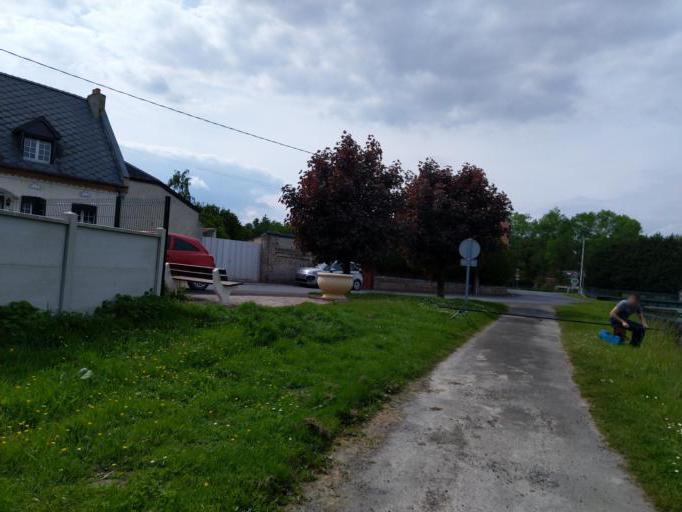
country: FR
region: Picardie
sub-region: Departement de l'Aisne
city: Etreux
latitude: 49.9537
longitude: 3.6066
